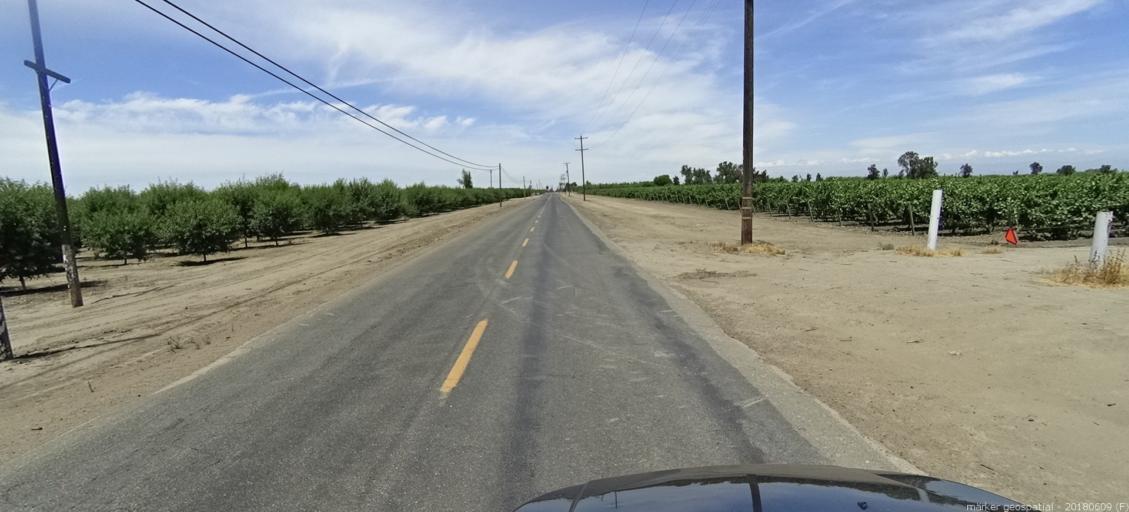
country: US
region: California
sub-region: Madera County
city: Parkwood
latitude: 36.8928
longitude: -120.0923
